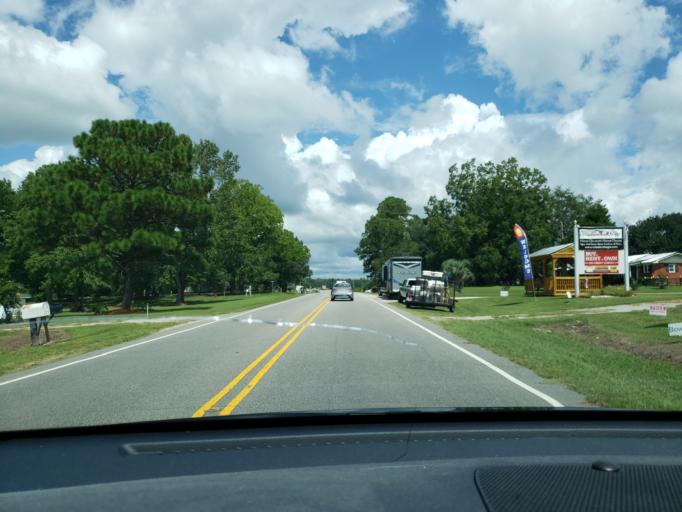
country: US
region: North Carolina
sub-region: Columbus County
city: Brunswick
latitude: 34.2698
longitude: -78.7419
